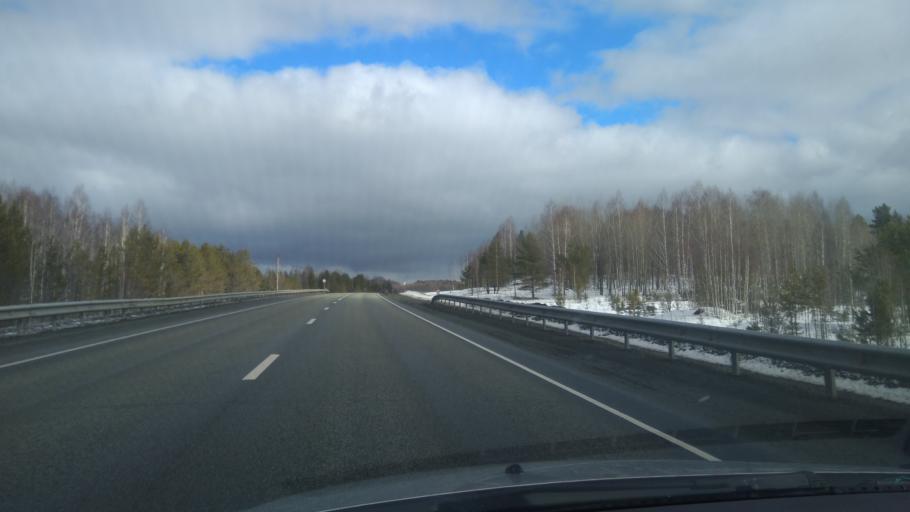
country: RU
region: Sverdlovsk
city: Bisert'
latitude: 56.8359
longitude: 58.8488
